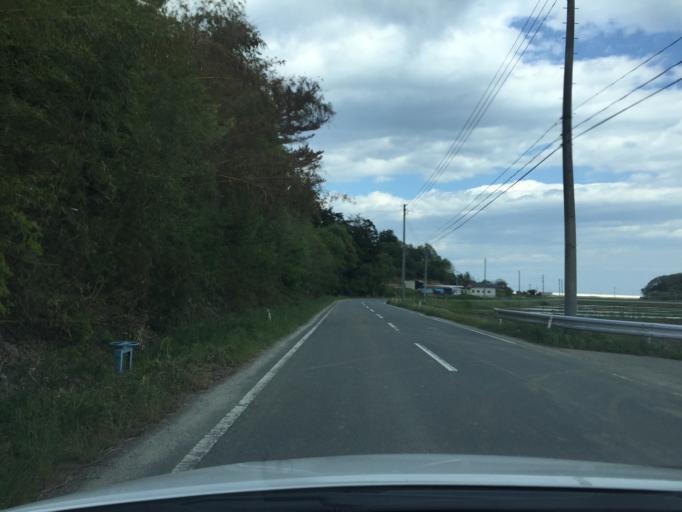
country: JP
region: Miyagi
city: Marumori
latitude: 37.7630
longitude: 140.9764
